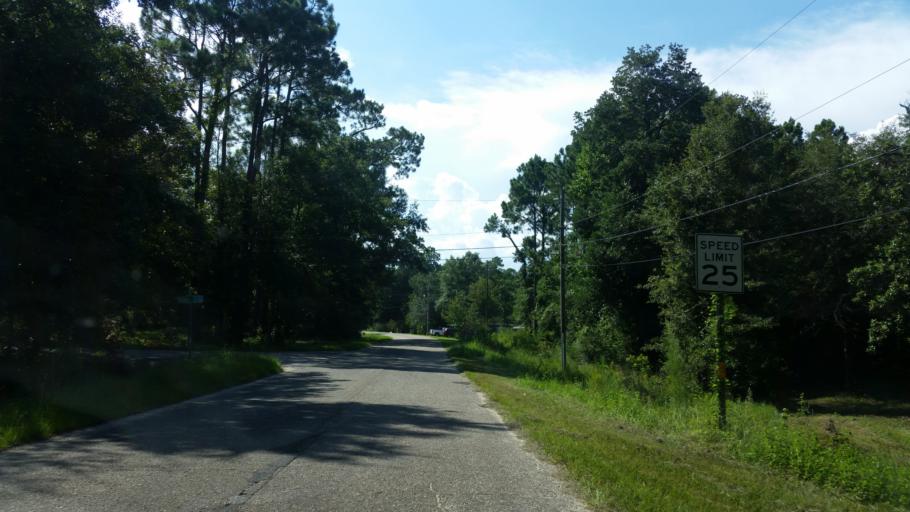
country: US
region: Florida
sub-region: Santa Rosa County
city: Pace
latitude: 30.5805
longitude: -87.1535
